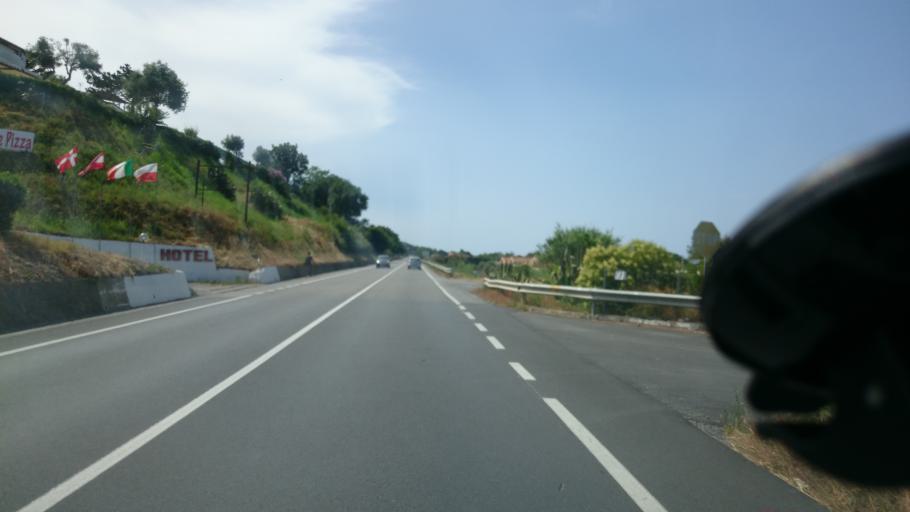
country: IT
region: Calabria
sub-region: Provincia di Cosenza
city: Diamante
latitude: 39.6973
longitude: 15.8148
